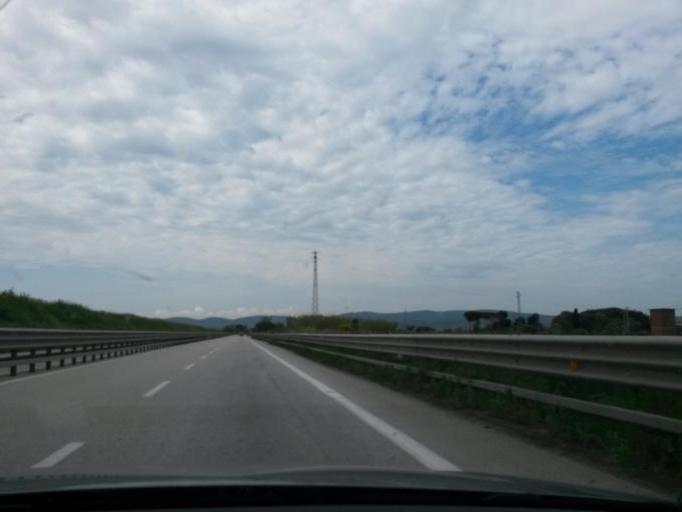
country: IT
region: Tuscany
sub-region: Provincia di Livorno
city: Venturina
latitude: 42.9929
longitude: 10.5739
